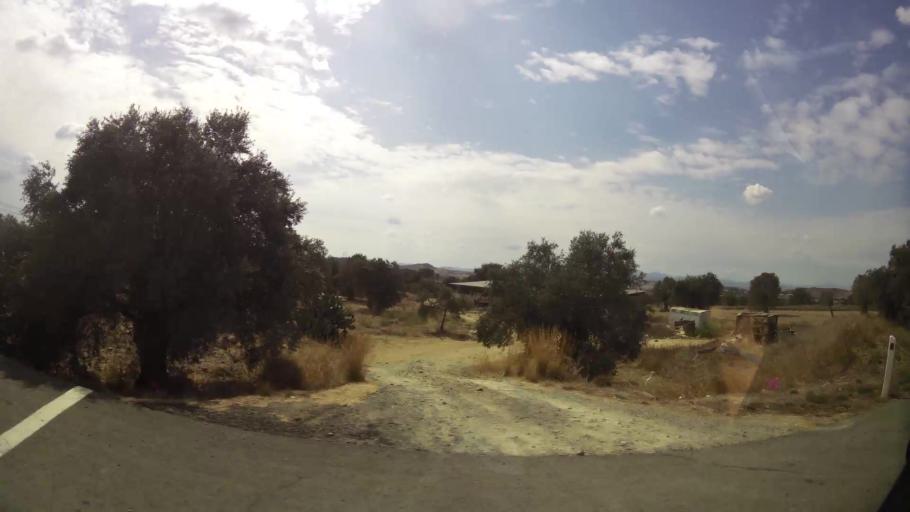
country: CY
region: Lefkosia
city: Tseri
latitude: 35.0647
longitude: 33.3408
